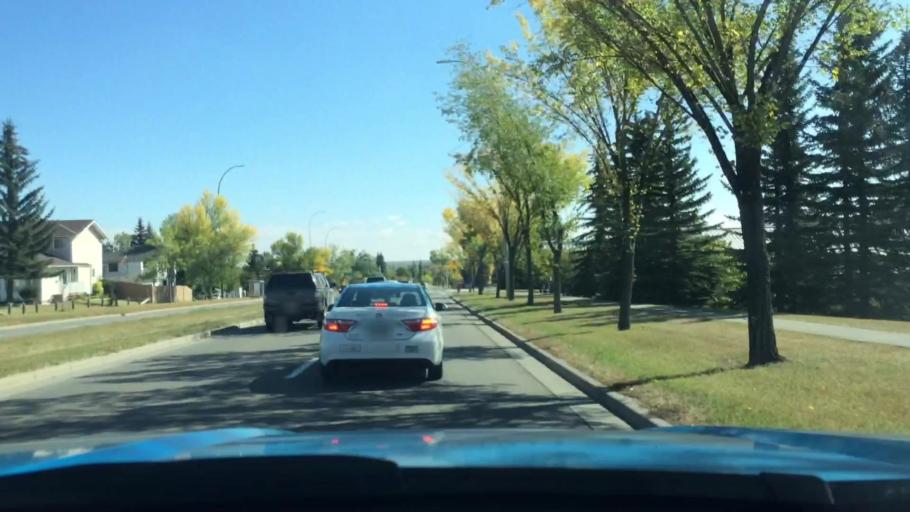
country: CA
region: Alberta
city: Calgary
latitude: 50.9140
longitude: -114.0851
